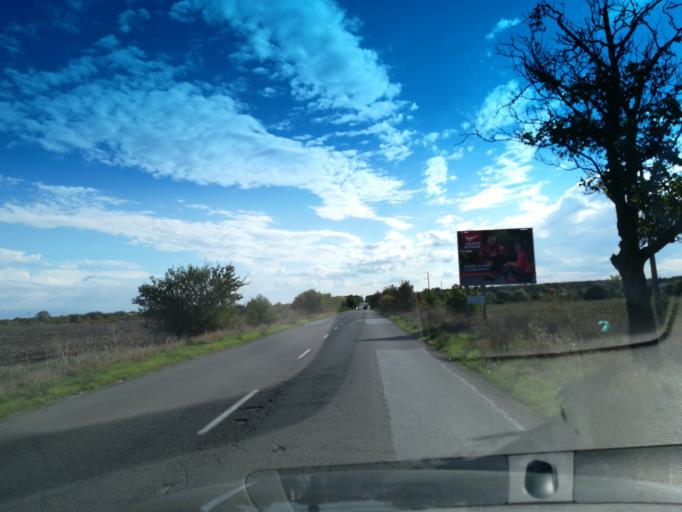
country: BG
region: Stara Zagora
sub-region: Obshtina Stara Zagora
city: Stara Zagora
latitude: 42.3648
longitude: 25.6547
